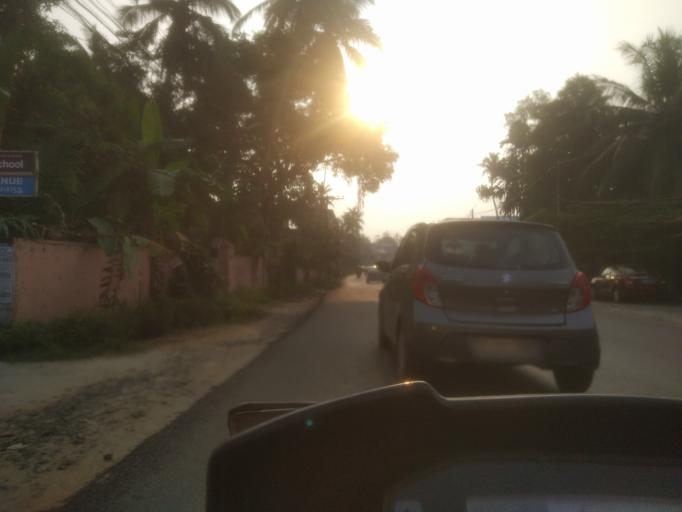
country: IN
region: Kerala
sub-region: Ernakulam
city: Cochin
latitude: 9.9393
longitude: 76.3300
